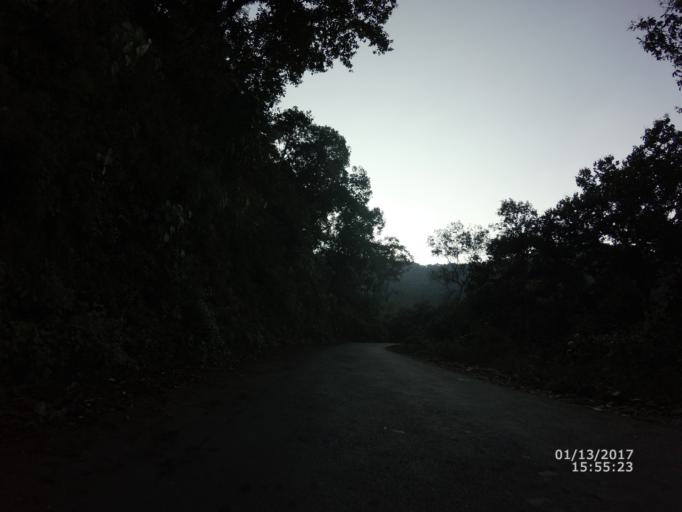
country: NP
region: Western Region
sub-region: Gandaki Zone
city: Pokhara
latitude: 28.1586
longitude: 84.0053
